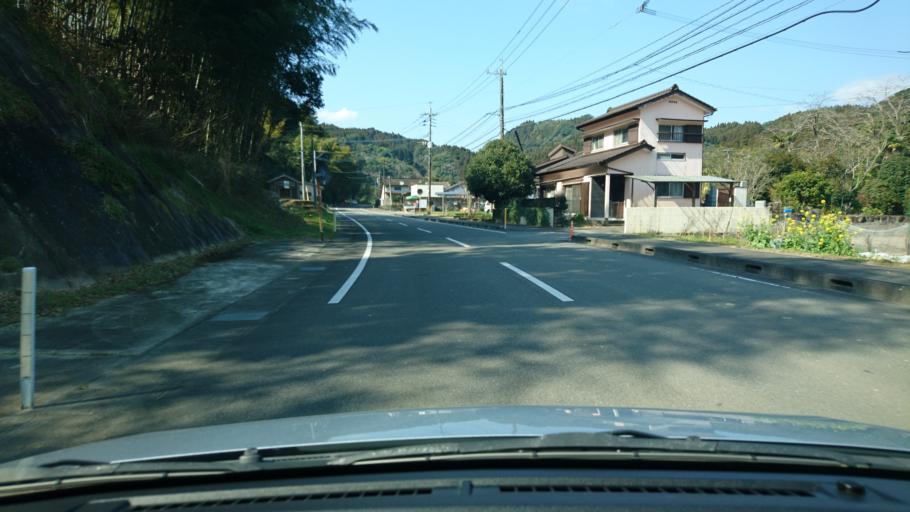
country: JP
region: Miyazaki
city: Miyazaki-shi
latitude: 31.8291
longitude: 131.4045
